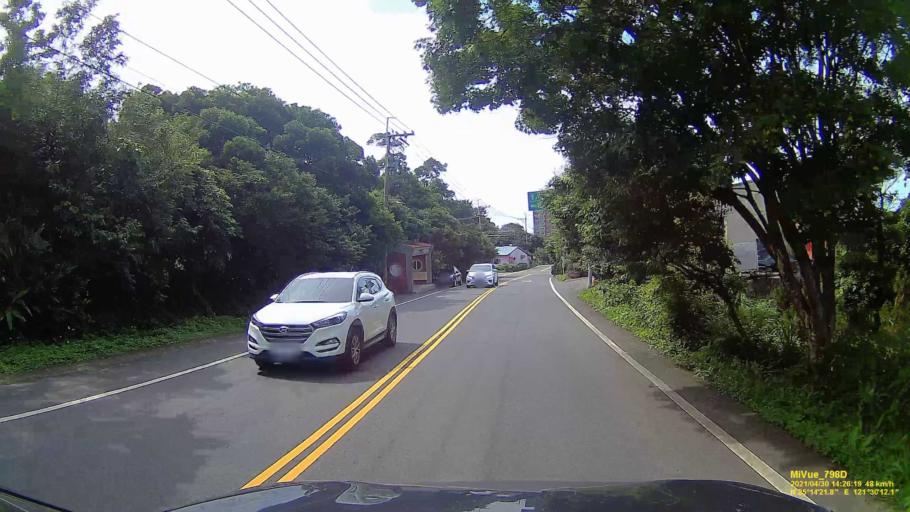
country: TW
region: Taipei
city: Taipei
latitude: 25.2396
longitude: 121.5032
